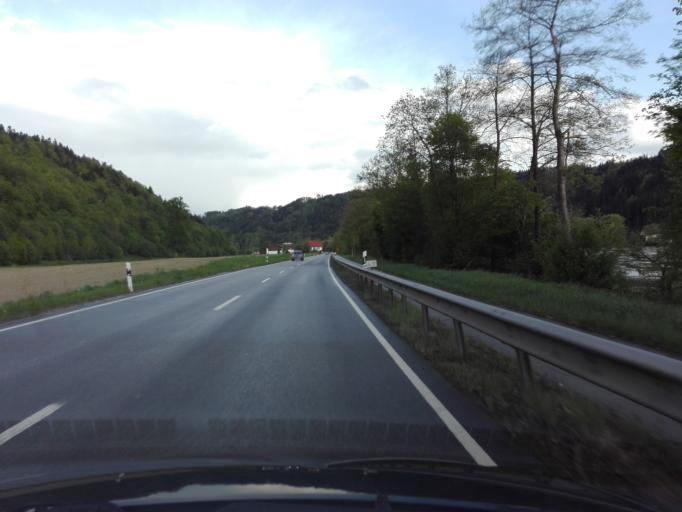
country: DE
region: Bavaria
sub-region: Lower Bavaria
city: Thyrnau
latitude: 48.5667
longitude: 13.5615
